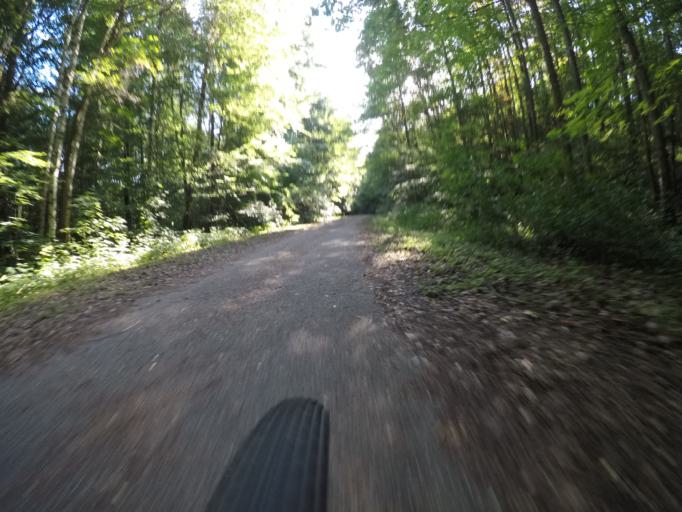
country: DE
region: Baden-Wuerttemberg
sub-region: Regierungsbezirk Stuttgart
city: Sindelfingen
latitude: 48.7291
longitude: 9.0639
